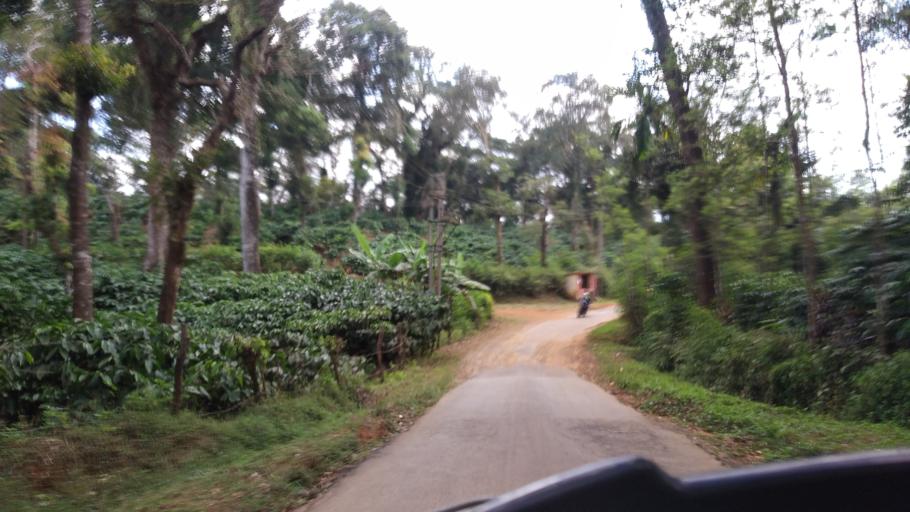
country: IN
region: Karnataka
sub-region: Kodagu
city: Ponnampet
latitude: 12.0369
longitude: 75.9103
